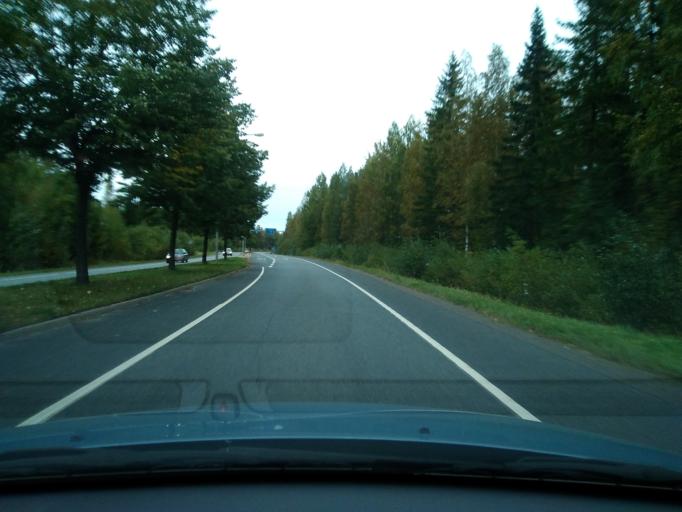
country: FI
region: Haeme
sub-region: Riihimaeki
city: Riihimaeki
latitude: 60.7528
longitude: 24.7450
